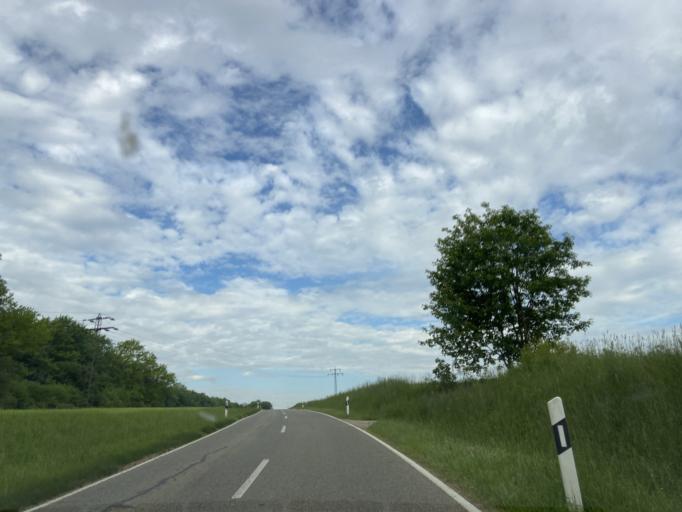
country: DE
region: Baden-Wuerttemberg
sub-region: Tuebingen Region
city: Ennetach
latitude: 48.0713
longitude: 9.3290
